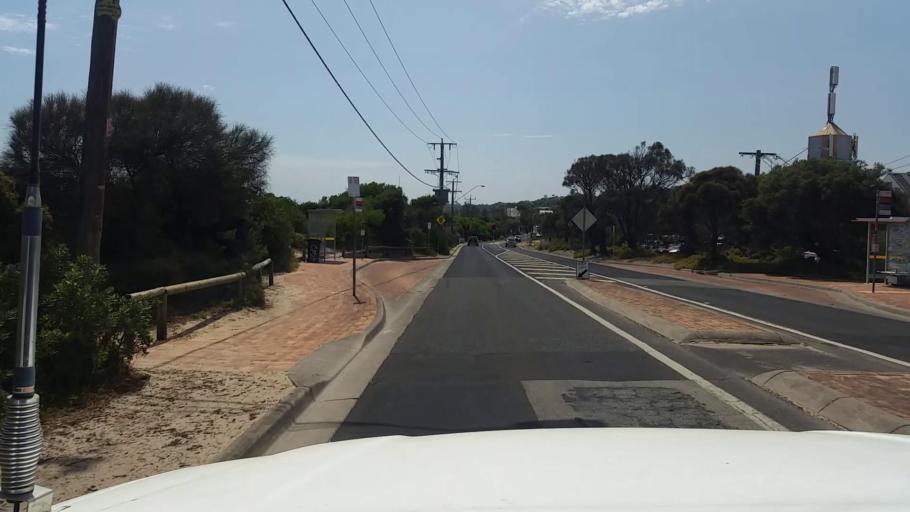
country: AU
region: Victoria
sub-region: Mornington Peninsula
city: Mount Martha
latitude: -38.2677
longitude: 145.0125
